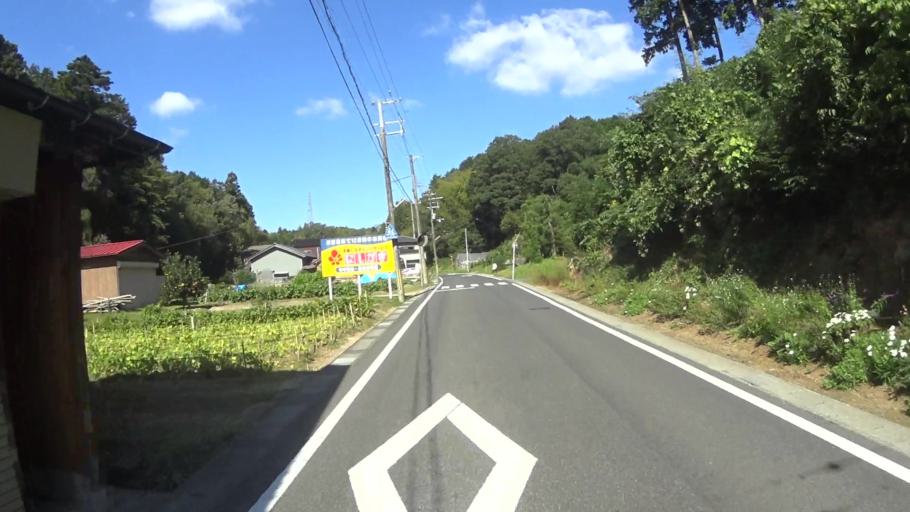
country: JP
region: Kyoto
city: Miyazu
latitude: 35.6334
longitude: 135.0724
